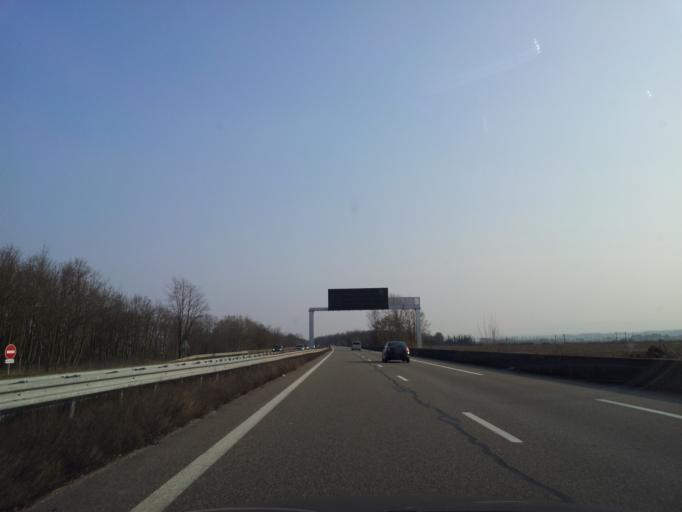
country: FR
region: Alsace
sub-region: Departement du Haut-Rhin
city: Bartenheim
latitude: 47.6291
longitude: 7.5051
